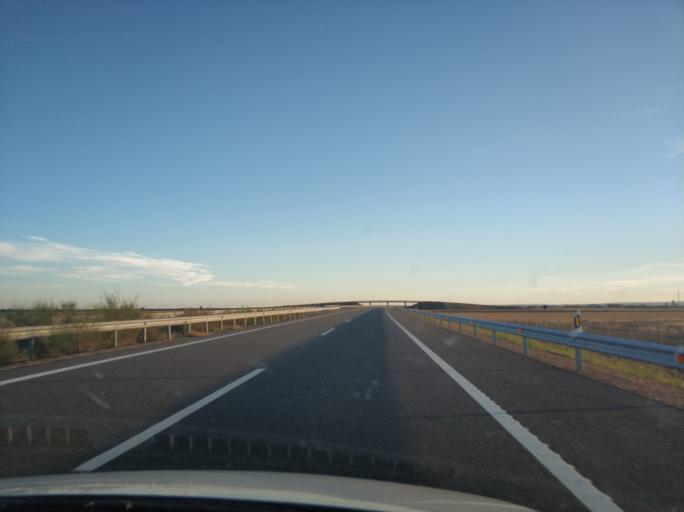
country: ES
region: Castille and Leon
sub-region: Provincia de Zamora
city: Barcial del Barco
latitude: 41.9379
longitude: -5.6423
